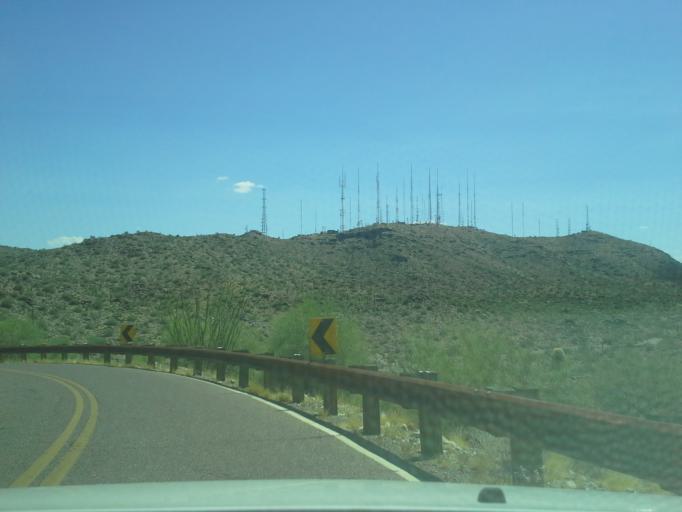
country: US
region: Arizona
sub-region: Maricopa County
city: Guadalupe
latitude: 33.3447
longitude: -112.0603
